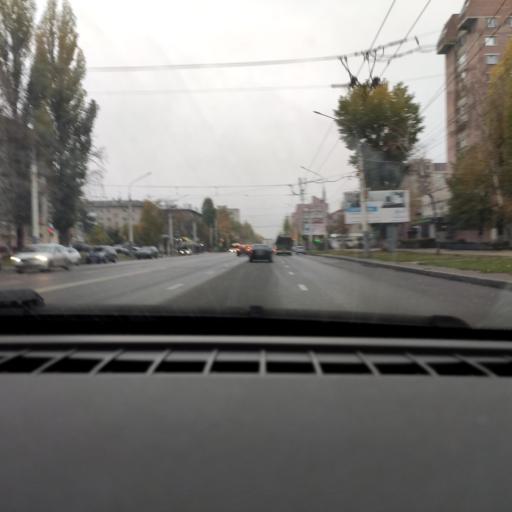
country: RU
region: Voronezj
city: Voronezh
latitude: 51.6539
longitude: 39.2430
